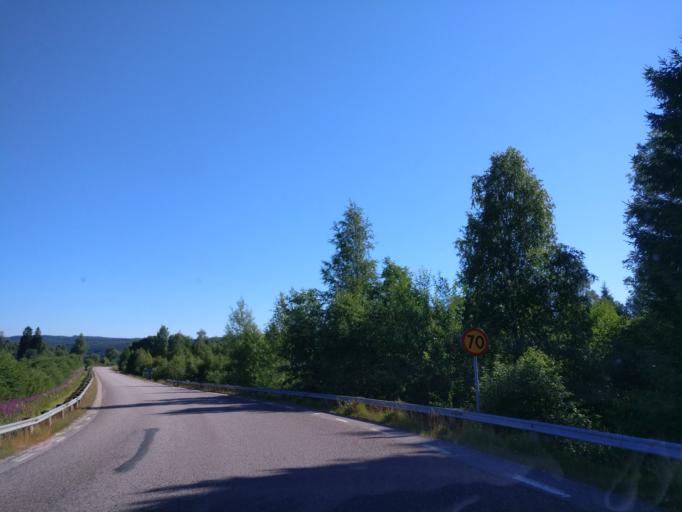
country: SE
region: Vaermland
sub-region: Hagfors Kommun
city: Hagfors
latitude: 60.0607
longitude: 13.5531
